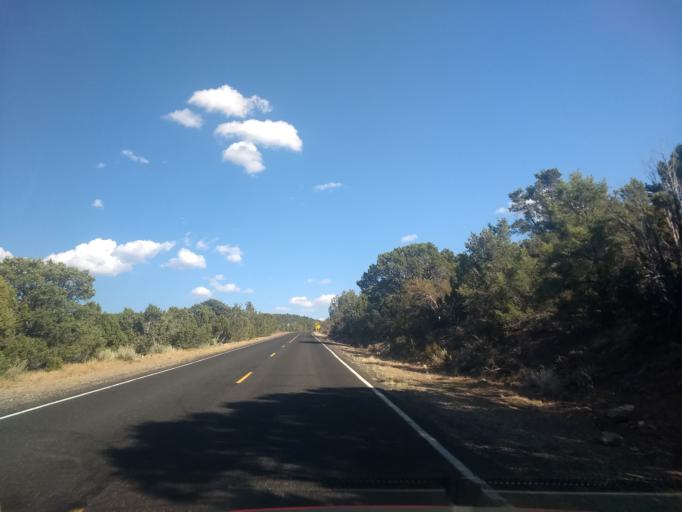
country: US
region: Utah
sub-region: Washington County
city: Enterprise
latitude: 37.4226
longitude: -113.5791
